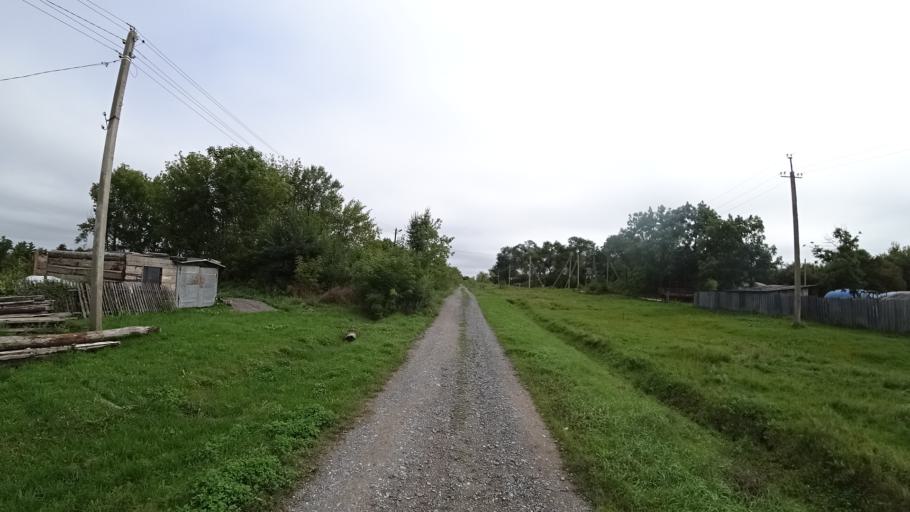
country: RU
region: Primorskiy
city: Lyalichi
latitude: 44.0786
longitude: 132.4778
